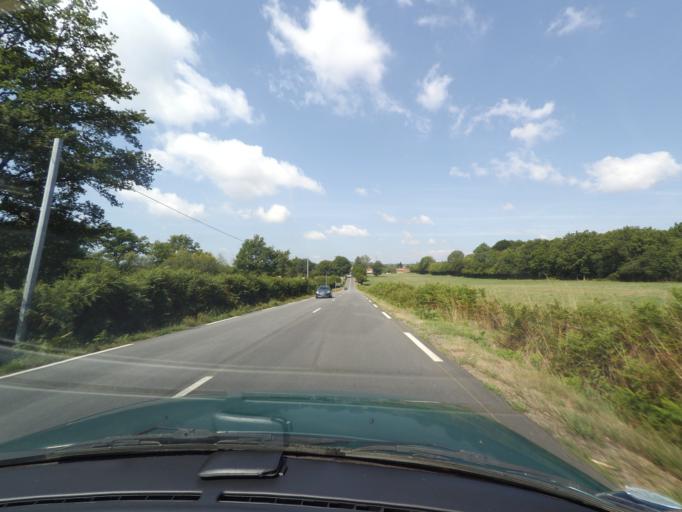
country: FR
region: Limousin
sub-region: Departement de la Haute-Vienne
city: Neuvic-Entier
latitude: 45.7613
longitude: 1.5775
